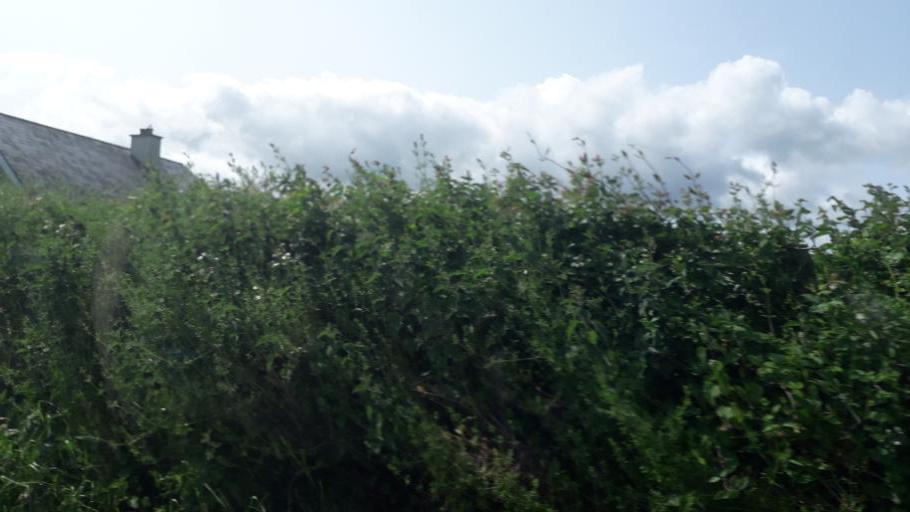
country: IE
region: Leinster
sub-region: Kilkenny
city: Graiguenamanagh
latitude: 52.6049
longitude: -7.0025
